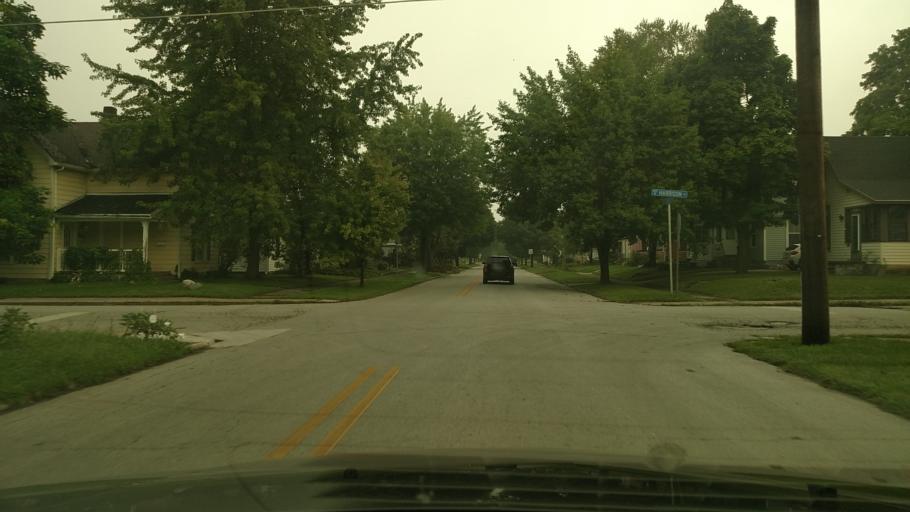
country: US
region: Indiana
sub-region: Howard County
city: Kokomo
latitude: 40.4786
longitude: -86.1365
